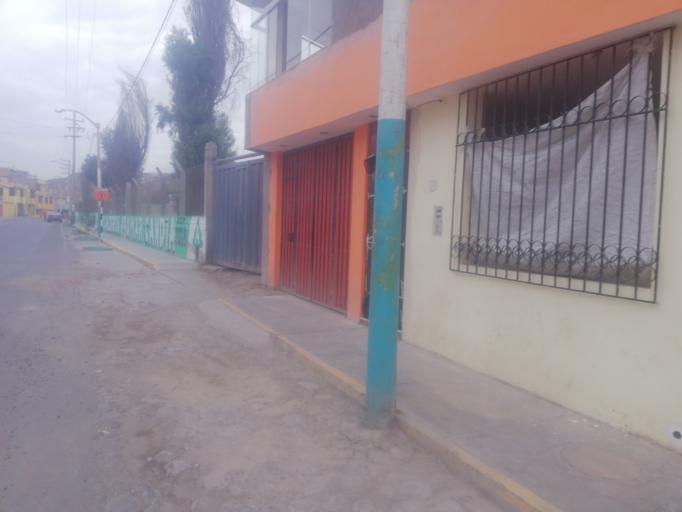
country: PE
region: Arequipa
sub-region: Provincia de Arequipa
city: Tiabaya
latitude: -16.4473
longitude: -71.5888
